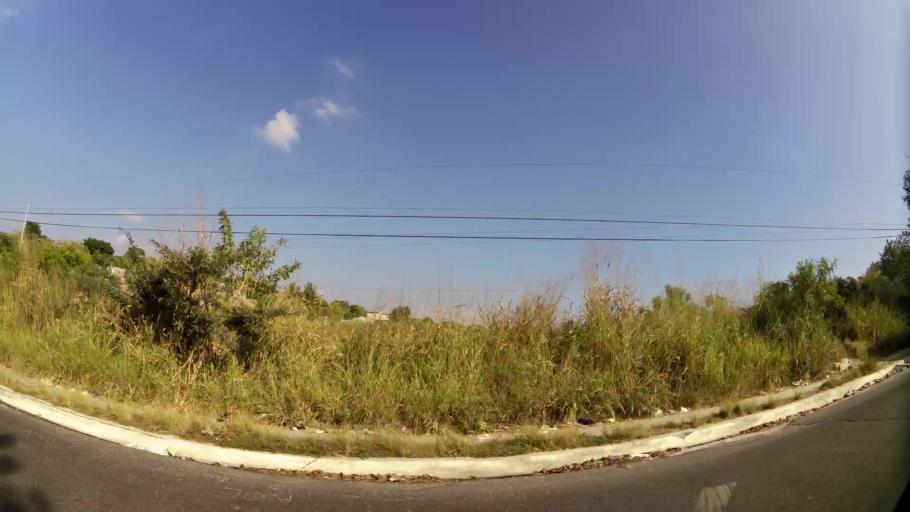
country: SV
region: San Salvador
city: Ilopango
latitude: 13.7211
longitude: -89.1061
